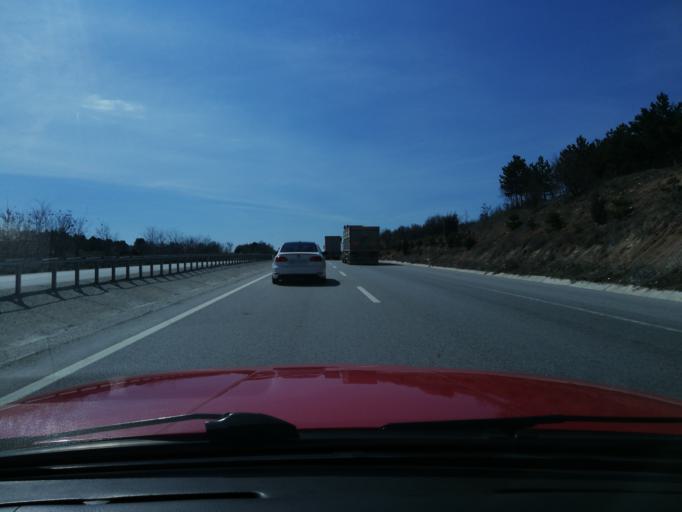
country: TR
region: Kuetahya
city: Kutahya
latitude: 39.3494
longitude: 30.0557
